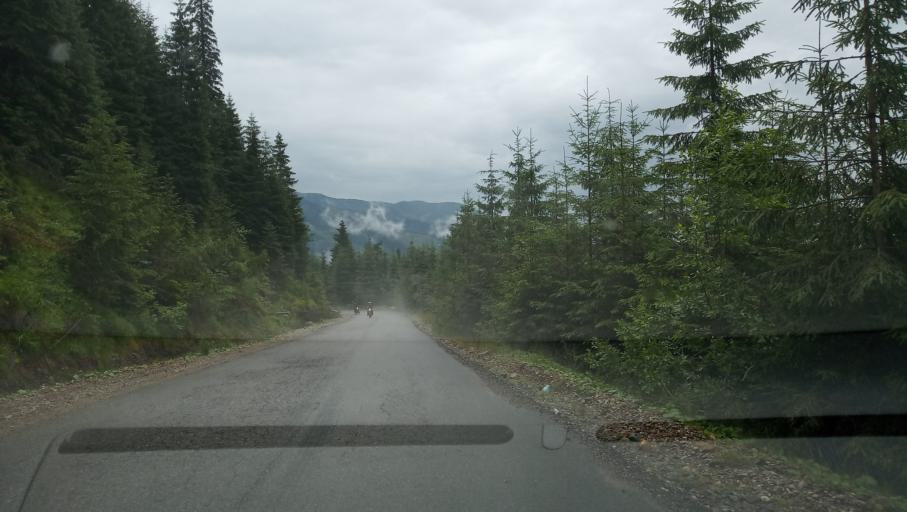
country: RO
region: Hunedoara
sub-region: Oras Petrila
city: Petrila
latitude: 45.4109
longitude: 23.5848
